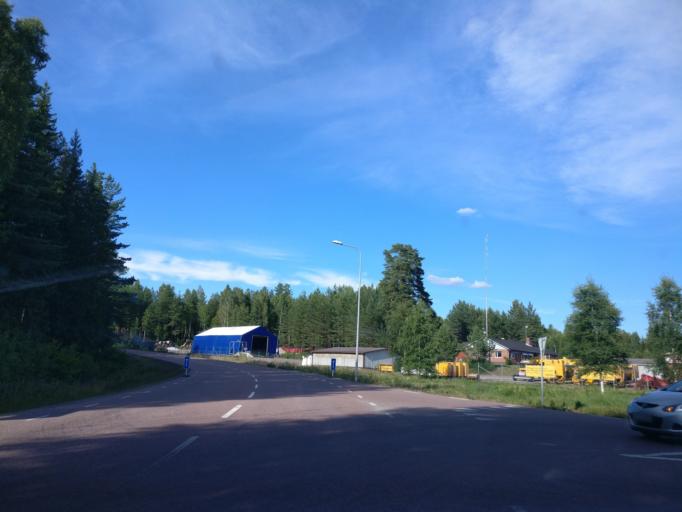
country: SE
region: Vaermland
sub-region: Arvika Kommun
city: Arvika
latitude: 59.6634
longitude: 12.6251
